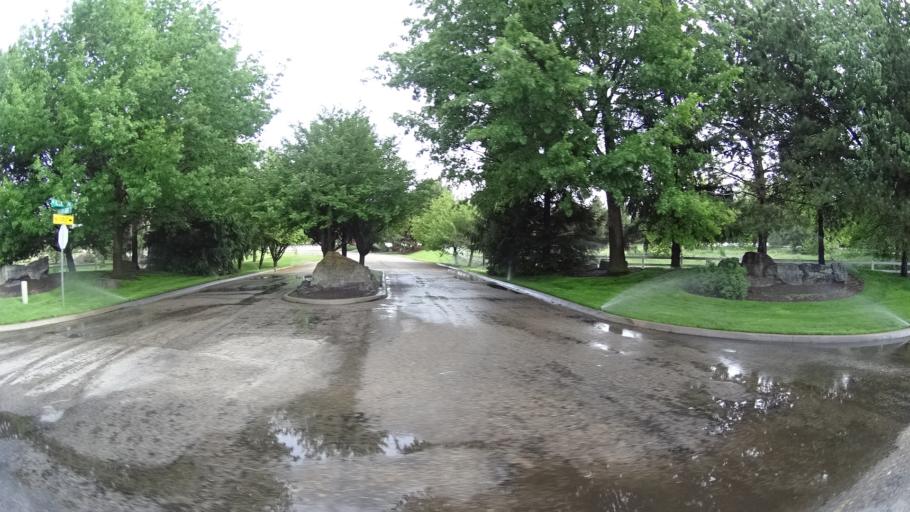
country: US
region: Idaho
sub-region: Ada County
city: Eagle
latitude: 43.7208
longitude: -116.3297
